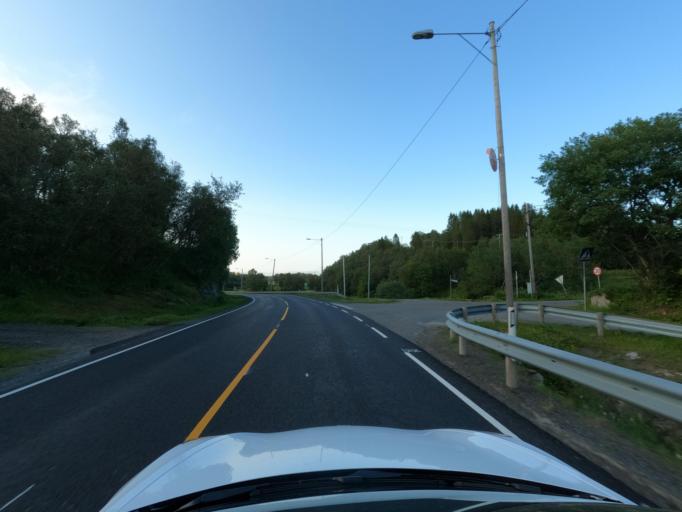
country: NO
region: Troms
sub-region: Skanland
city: Evenskjer
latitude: 68.6658
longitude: 16.5753
